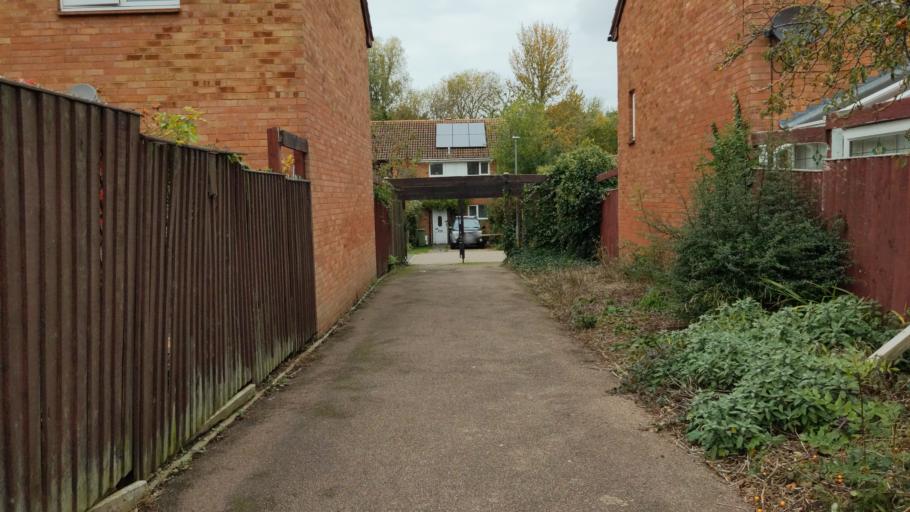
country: GB
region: England
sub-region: Buckinghamshire
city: Bletchley
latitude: 52.0103
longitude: -0.7598
